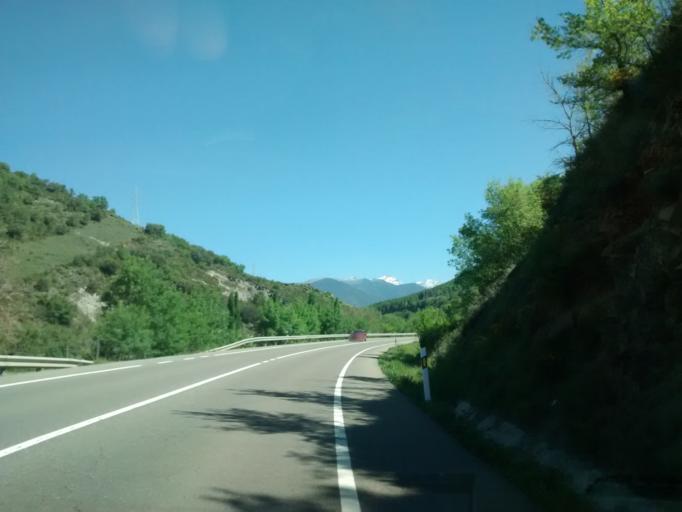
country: ES
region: Aragon
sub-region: Provincia de Huesca
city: Castiello de Jaca
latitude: 42.6021
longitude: -0.5439
